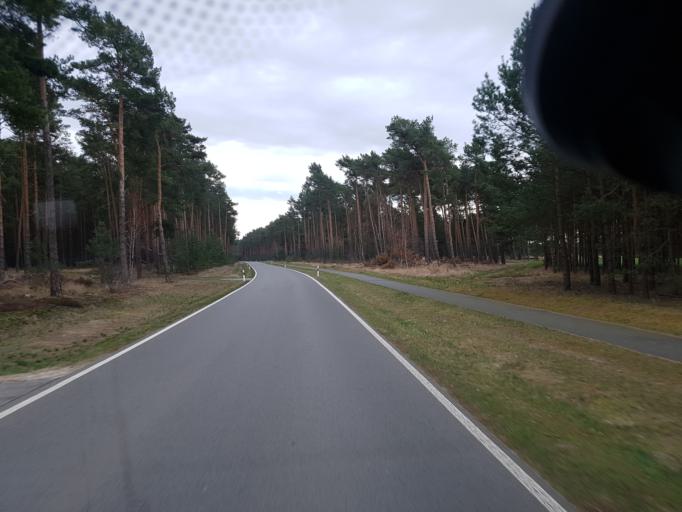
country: DE
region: Brandenburg
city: Mixdorf
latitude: 52.2004
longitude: 14.3765
